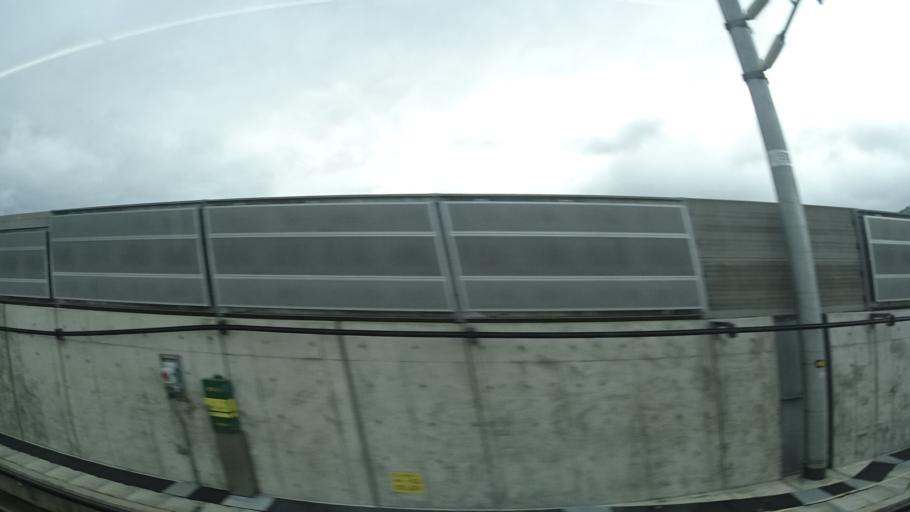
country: JP
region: Nagano
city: Iiyama
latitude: 36.8420
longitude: 138.3617
